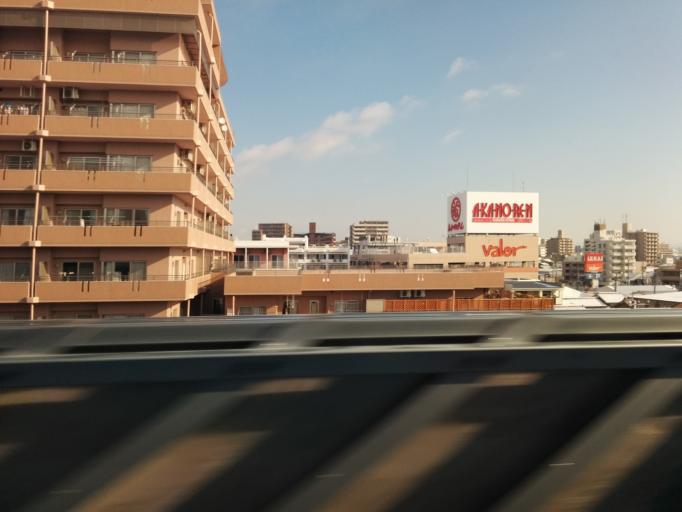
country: JP
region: Aichi
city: Nagoya-shi
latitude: 35.1125
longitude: 136.9026
